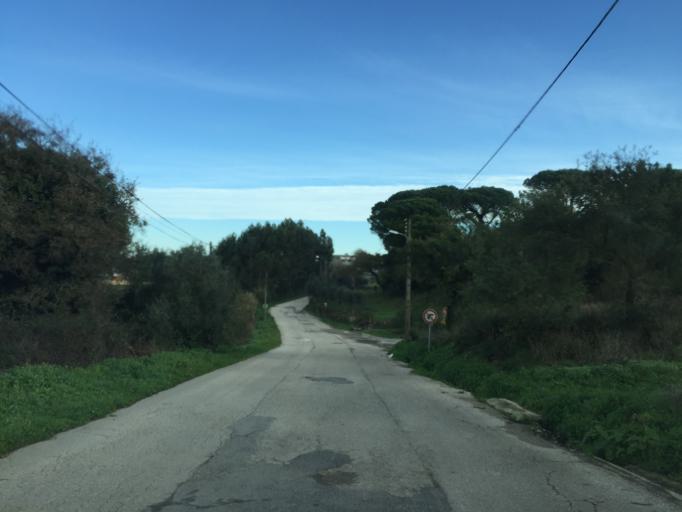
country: PT
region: Lisbon
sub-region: Odivelas
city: Canecas
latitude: 38.8215
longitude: -9.2472
